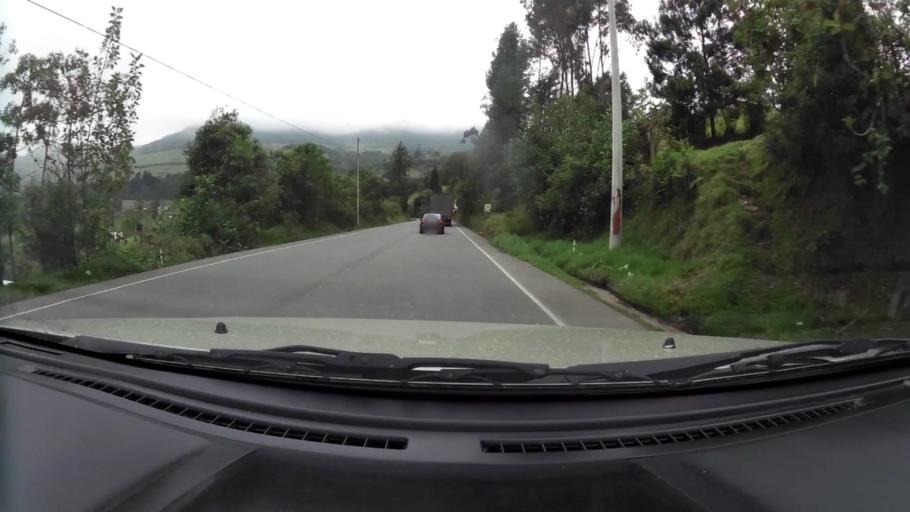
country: EC
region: Canar
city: Canar
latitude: -2.3842
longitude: -78.9702
